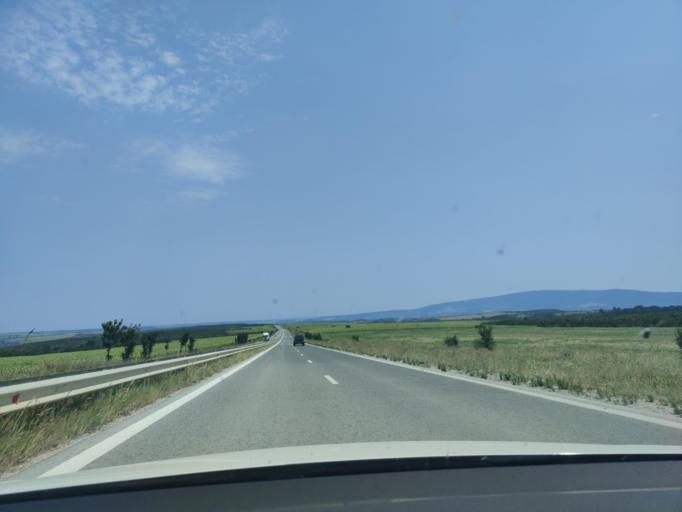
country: BG
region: Montana
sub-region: Obshtina Montana
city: Montana
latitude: 43.4252
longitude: 23.1685
